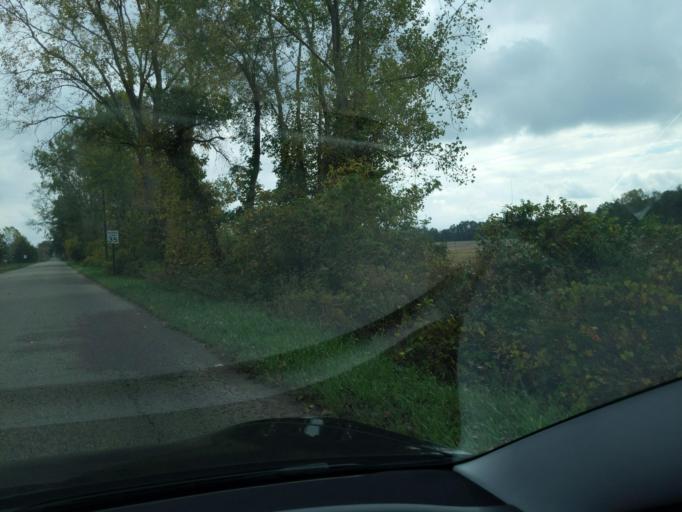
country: US
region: Michigan
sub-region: Eaton County
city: Eaton Rapids
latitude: 42.4929
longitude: -84.6545
